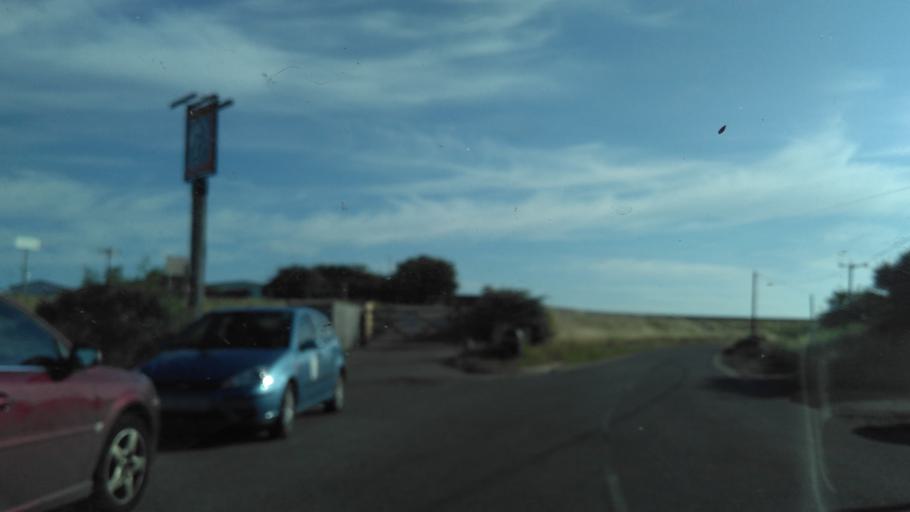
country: GB
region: England
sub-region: Kent
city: Dunkirk
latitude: 51.3442
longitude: 0.9594
